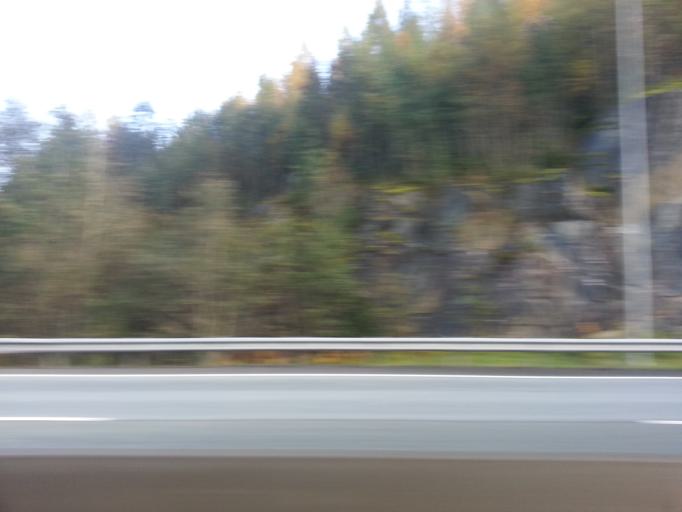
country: NO
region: Sor-Trondelag
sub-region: Malvik
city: Hommelvik
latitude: 63.4052
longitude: 10.8153
